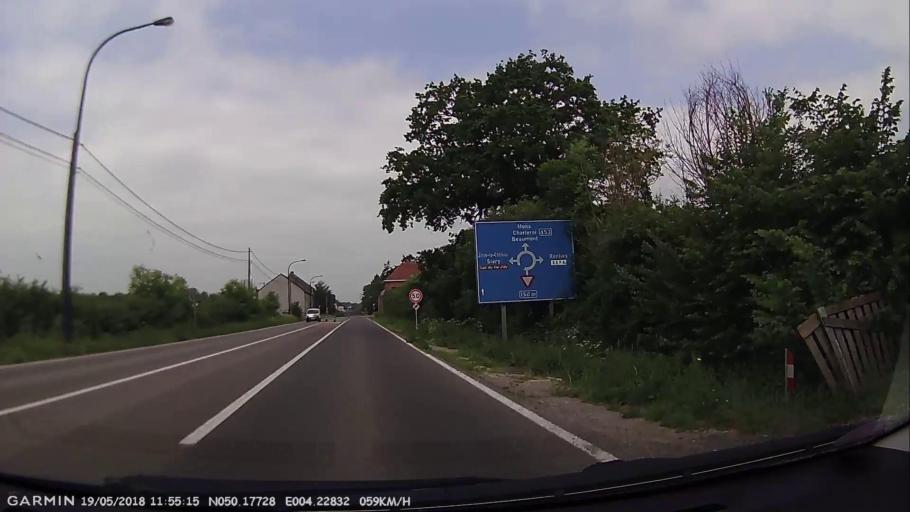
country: BE
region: Wallonia
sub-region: Province du Hainaut
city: Beaumont
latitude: 50.1774
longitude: 4.2282
